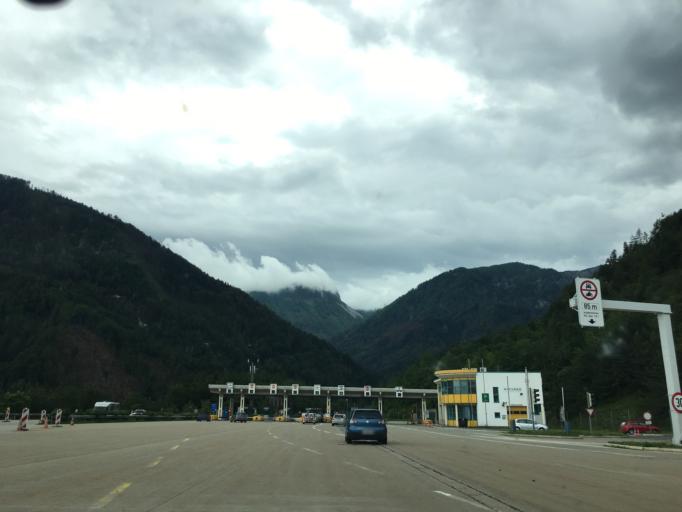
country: AT
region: Carinthia
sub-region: Politischer Bezirk Villach Land
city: Sankt Jakob
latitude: 46.5282
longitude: 14.0308
